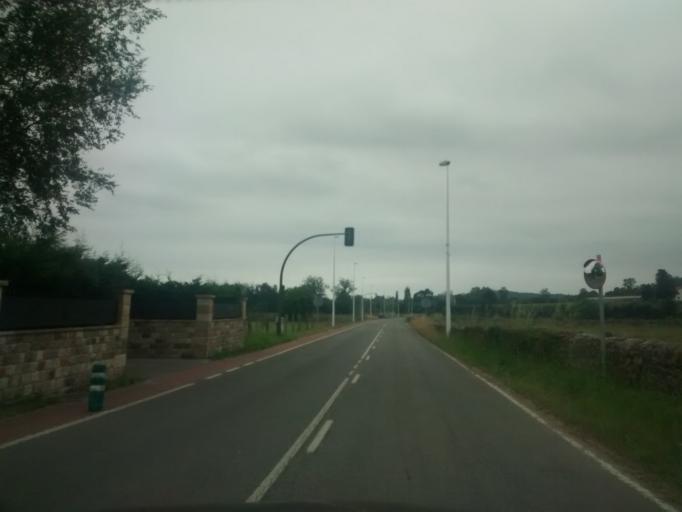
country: ES
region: Cantabria
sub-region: Provincia de Cantabria
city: Luzmela
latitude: 43.2918
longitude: -4.2206
